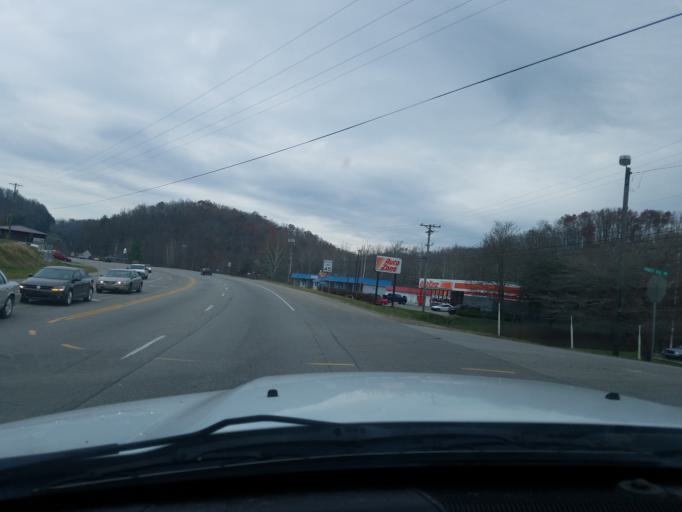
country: US
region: Kentucky
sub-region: Rowan County
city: Morehead
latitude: 38.1872
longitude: -83.4764
